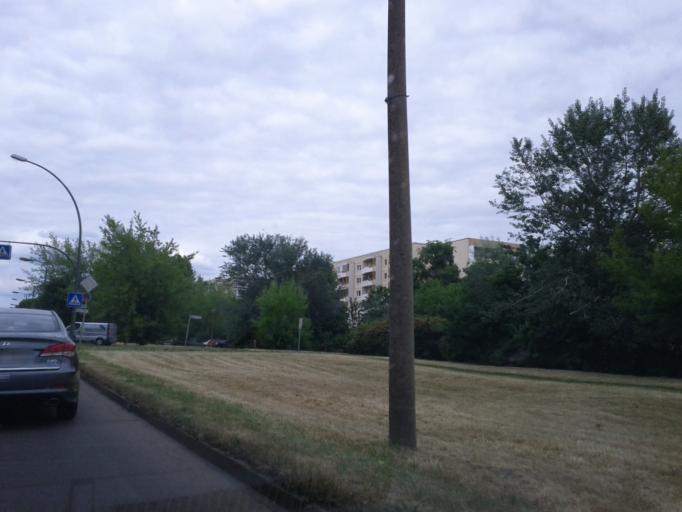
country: DE
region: Berlin
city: Marzahn
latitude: 52.5519
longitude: 13.5734
